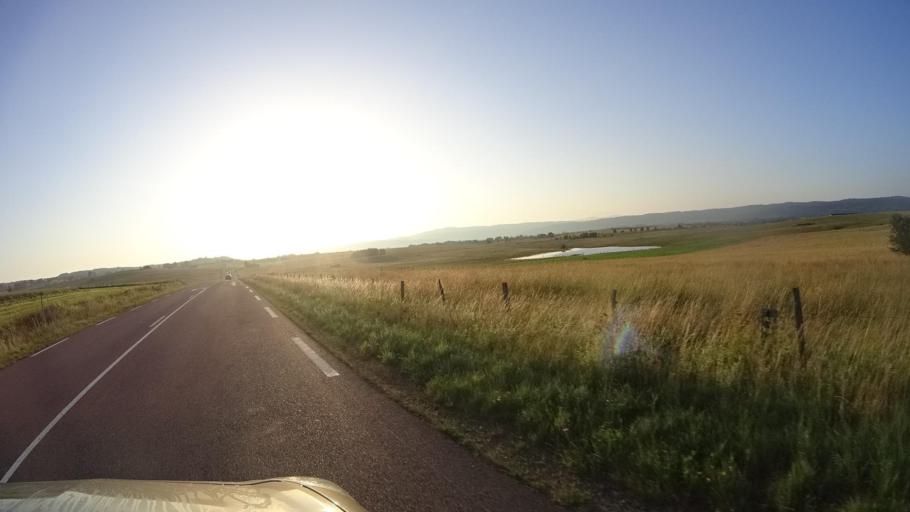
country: FR
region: Franche-Comte
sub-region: Departement du Doubs
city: Frasne
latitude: 46.9013
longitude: 6.2498
